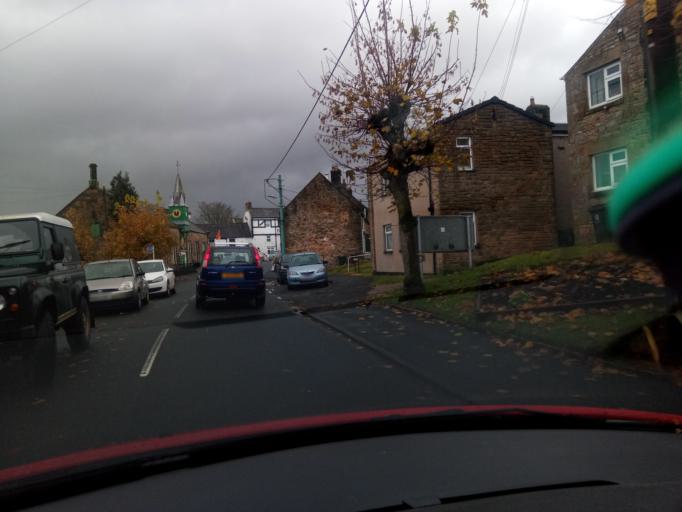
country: GB
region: England
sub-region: Northumberland
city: Birtley
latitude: 55.1440
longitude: -2.2547
